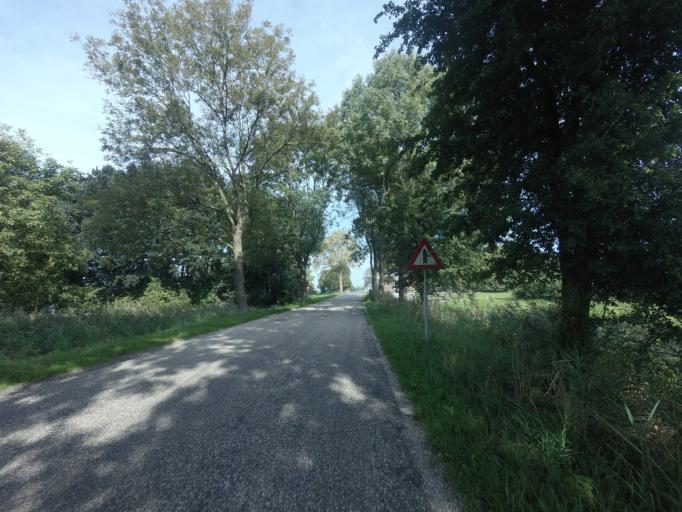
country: NL
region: Groningen
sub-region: Gemeente Leek
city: Leek
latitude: 53.2009
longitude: 6.3505
